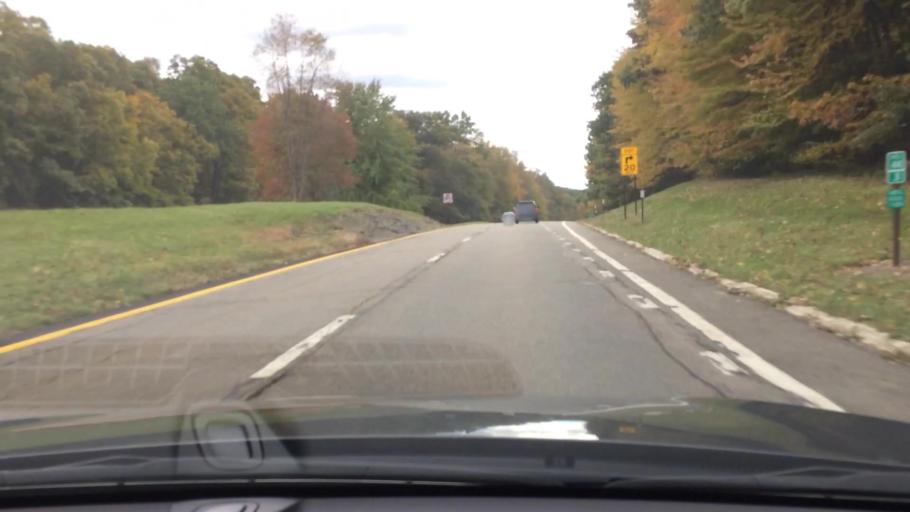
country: US
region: New York
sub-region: Dutchess County
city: Hillside Lake
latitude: 41.6352
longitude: -73.7828
